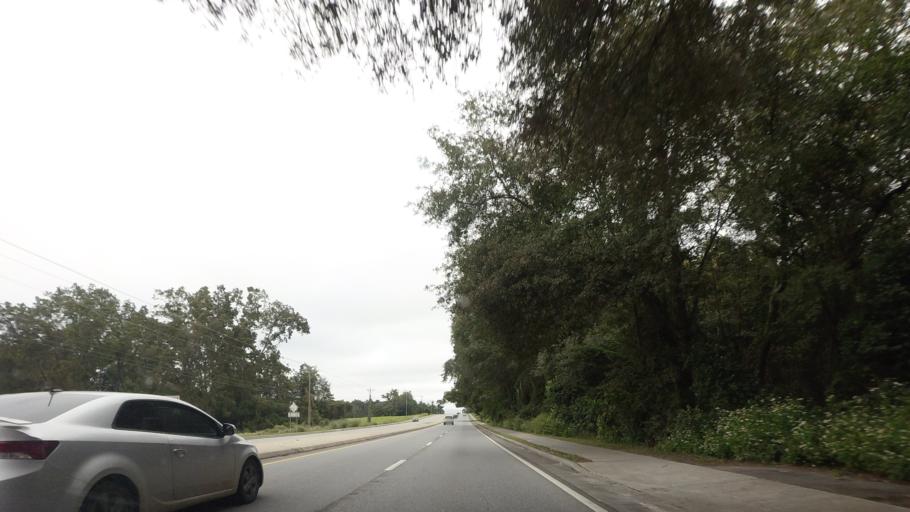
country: US
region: Georgia
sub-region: Lowndes County
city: Valdosta
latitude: 30.8982
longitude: -83.2675
